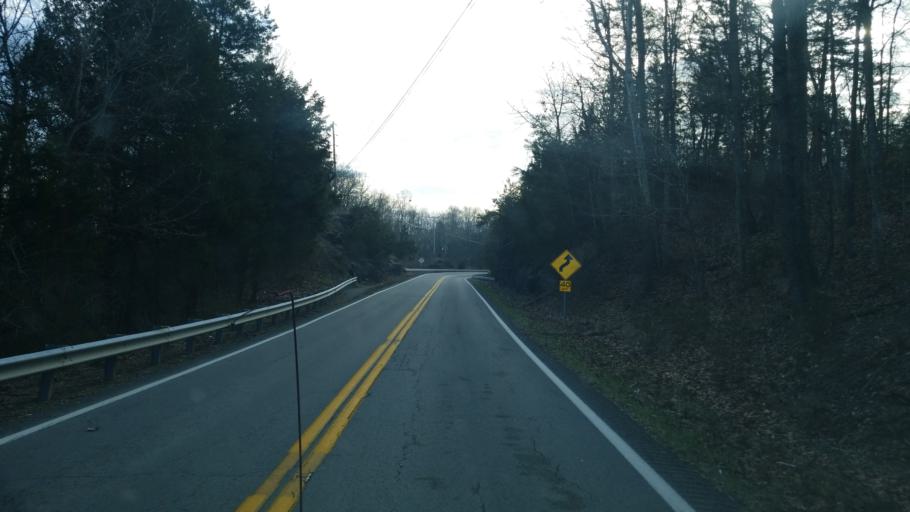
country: US
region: Kentucky
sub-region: Russell County
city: Jamestown
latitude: 36.8712
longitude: -85.1234
